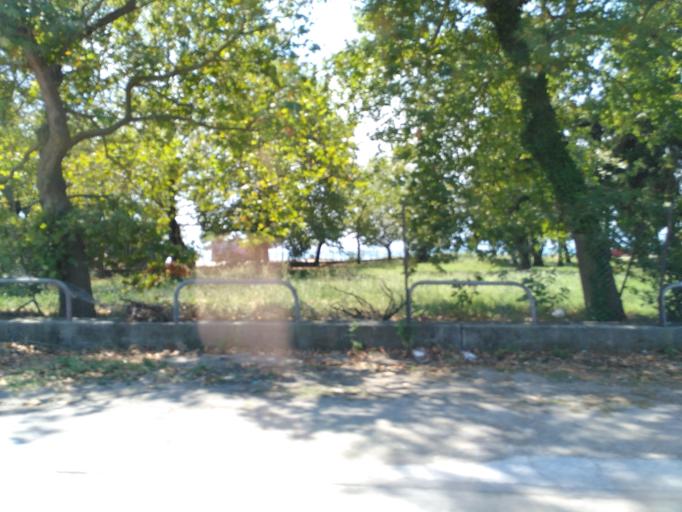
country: GR
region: Central Macedonia
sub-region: Nomos Thessalonikis
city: Nea Michaniona
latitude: 40.4285
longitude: 22.8800
